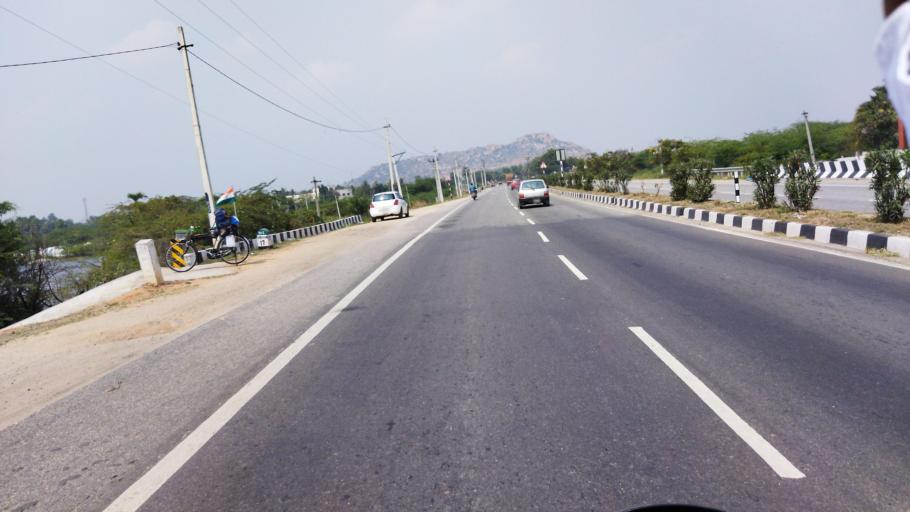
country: IN
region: Telangana
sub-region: Nalgonda
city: Nalgonda
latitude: 17.0815
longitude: 79.2769
